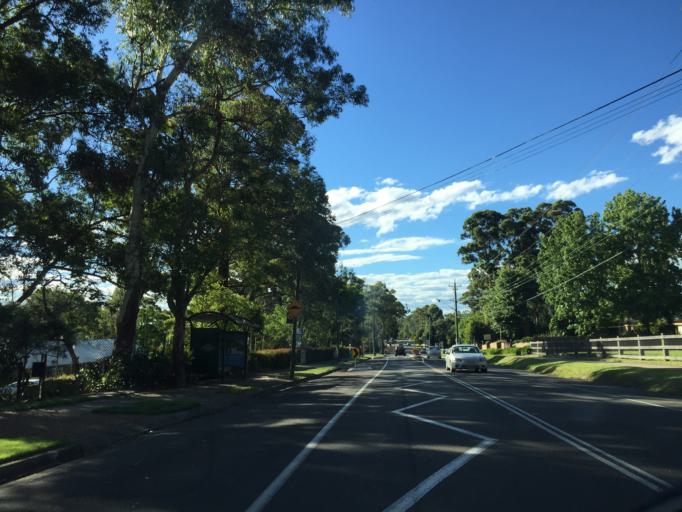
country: AU
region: New South Wales
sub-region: The Hills Shire
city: Glenhaven
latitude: -33.7009
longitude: 151.0041
